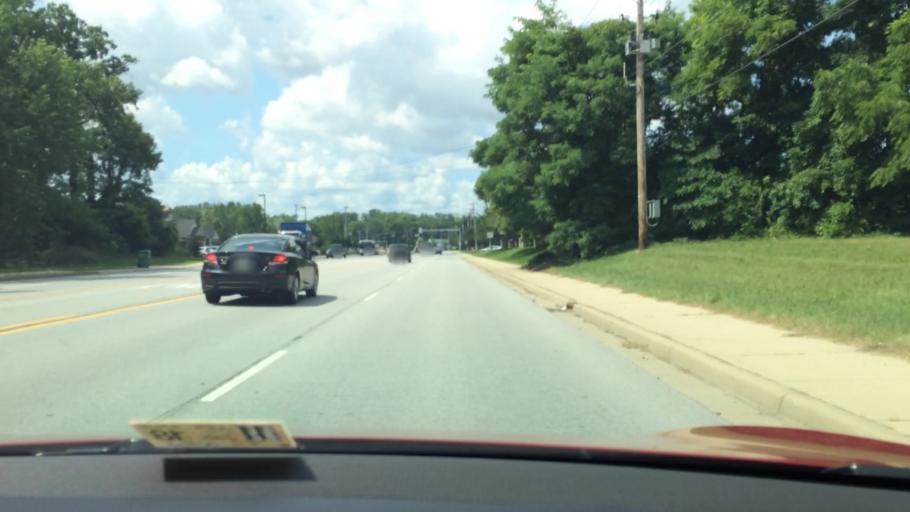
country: US
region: Indiana
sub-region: Saint Joseph County
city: Georgetown
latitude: 41.7116
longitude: -86.2018
